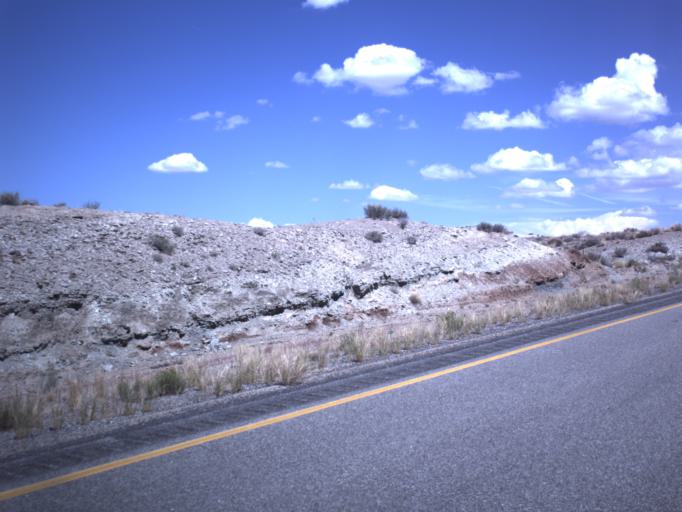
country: US
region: Utah
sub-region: Emery County
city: Ferron
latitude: 38.8469
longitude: -111.0199
